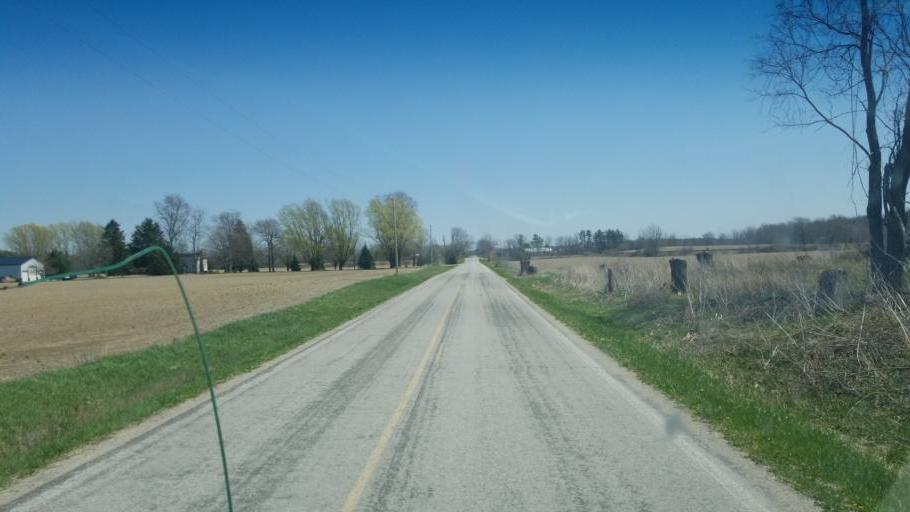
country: US
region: Ohio
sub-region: Huron County
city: New London
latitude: 41.1020
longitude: -82.3663
